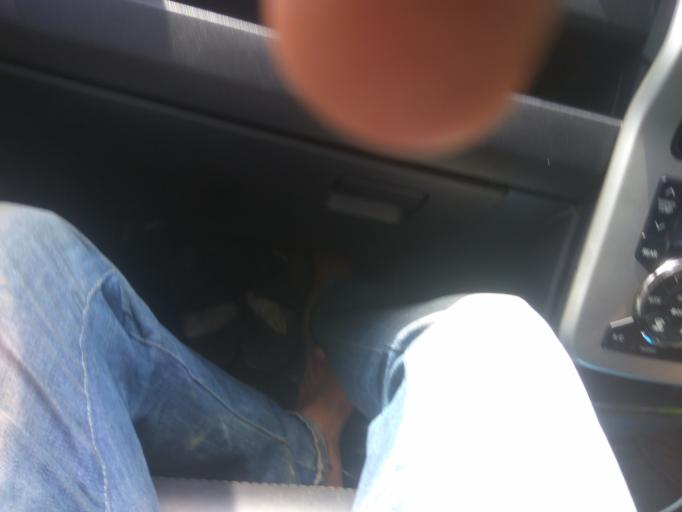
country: IN
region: Assam
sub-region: Karimganj
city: Karimganj
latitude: 24.8116
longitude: 92.1815
